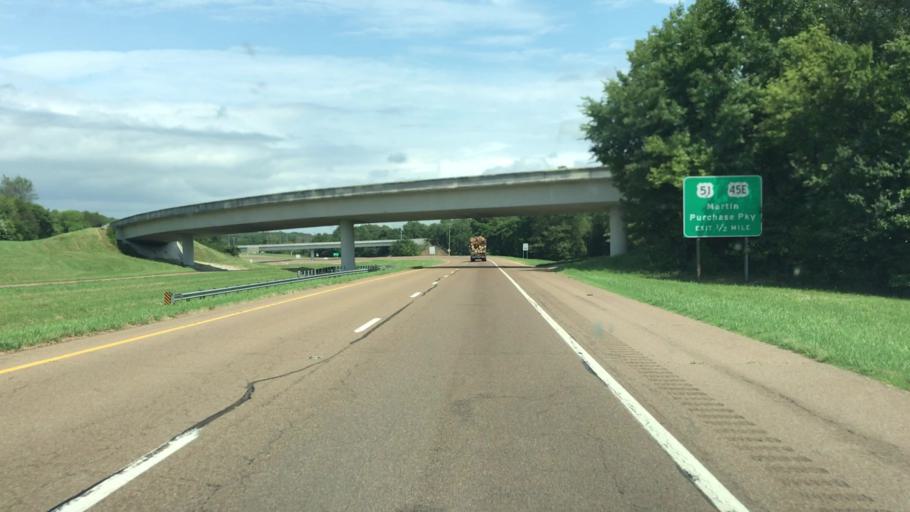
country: US
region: Tennessee
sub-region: Obion County
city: South Fulton
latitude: 36.4948
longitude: -88.9099
